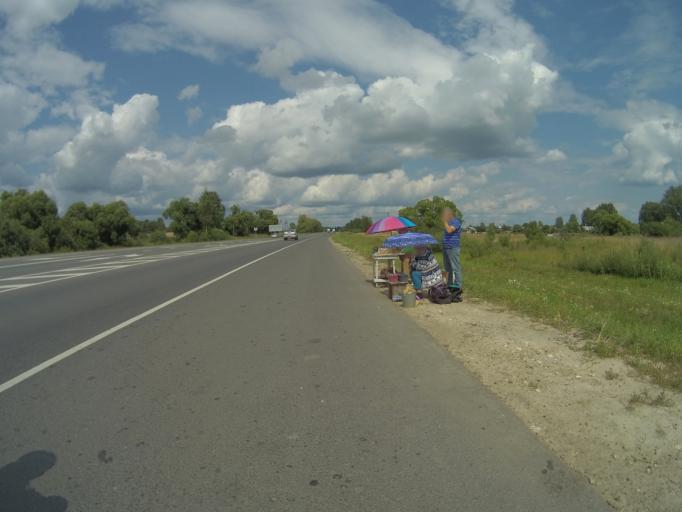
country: RU
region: Vladimir
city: Kideksha
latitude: 56.5591
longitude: 40.5484
